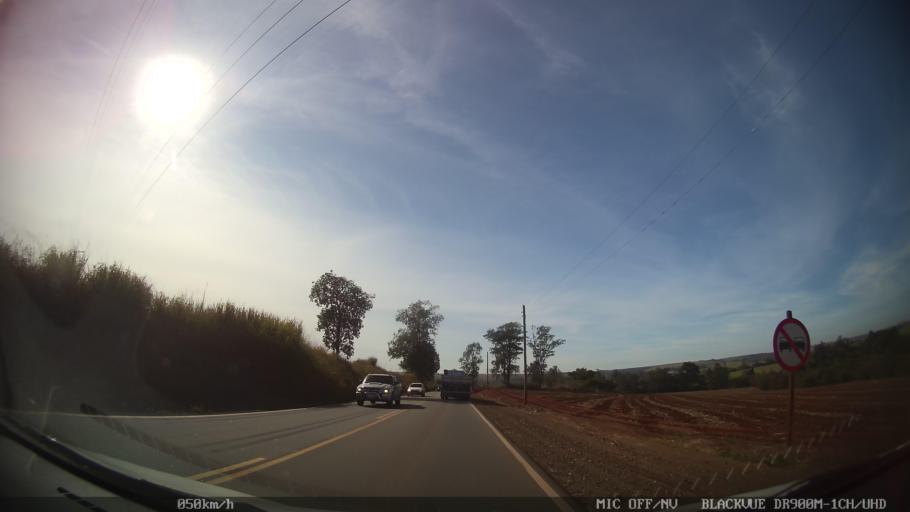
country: BR
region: Sao Paulo
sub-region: Rio Das Pedras
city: Rio das Pedras
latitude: -22.7895
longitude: -47.6389
